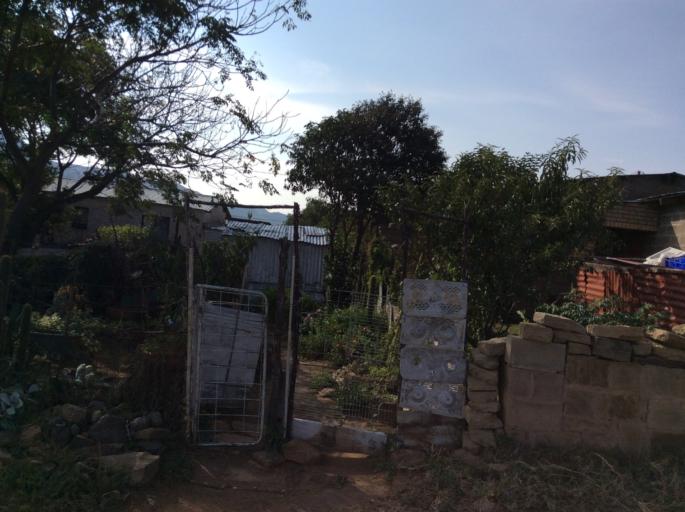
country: LS
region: Mafeteng
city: Mafeteng
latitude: -29.7189
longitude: 27.0114
